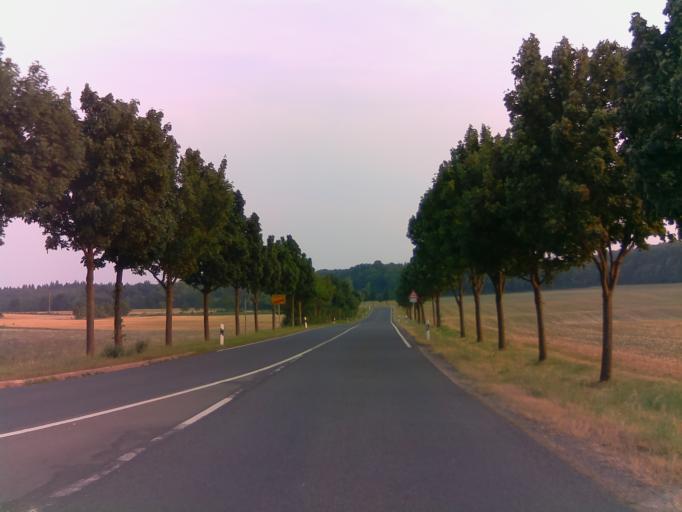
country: DE
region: Thuringia
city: Troistedt
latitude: 50.9369
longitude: 11.2461
